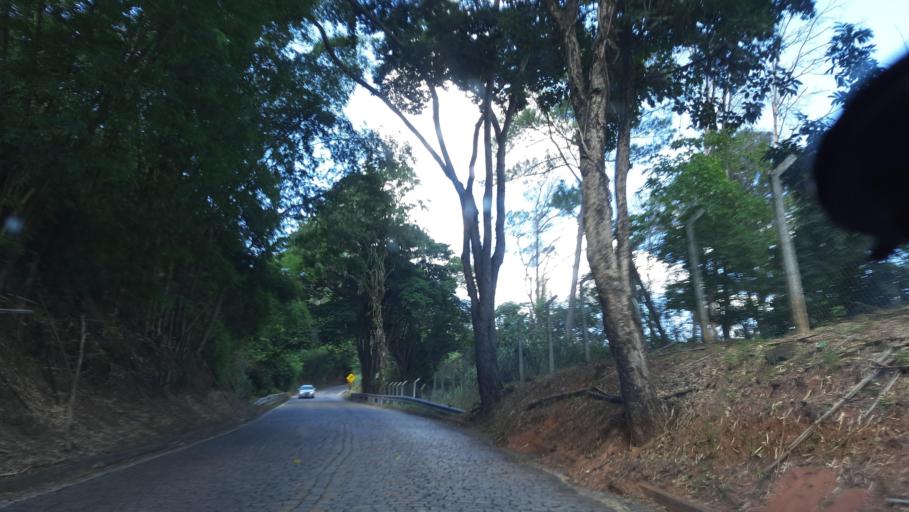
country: BR
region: Sao Paulo
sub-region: Sao Jose Do Rio Pardo
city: Sao Jose do Rio Pardo
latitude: -21.6030
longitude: -46.9531
